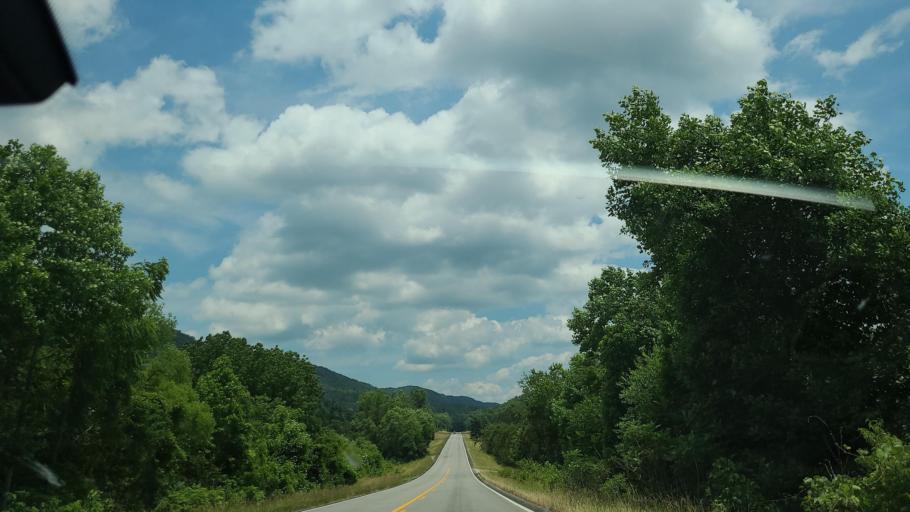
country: US
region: Tennessee
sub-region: Cumberland County
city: Lake Tansi
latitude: 35.7364
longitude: -85.0758
